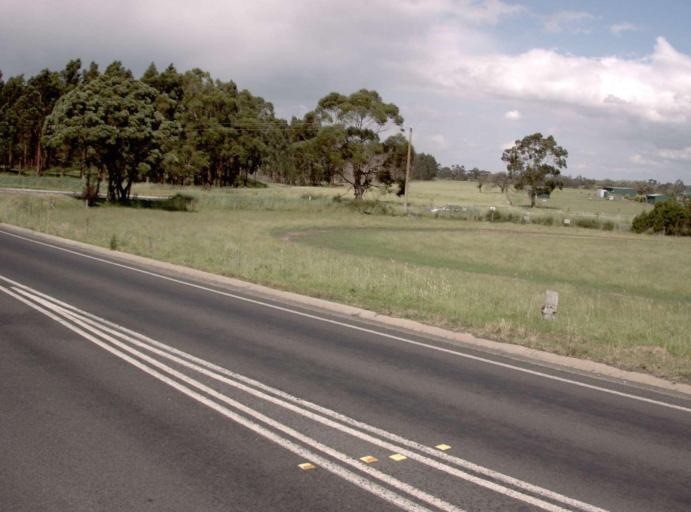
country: AU
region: Victoria
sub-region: Latrobe
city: Morwell
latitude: -38.1618
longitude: 146.4059
